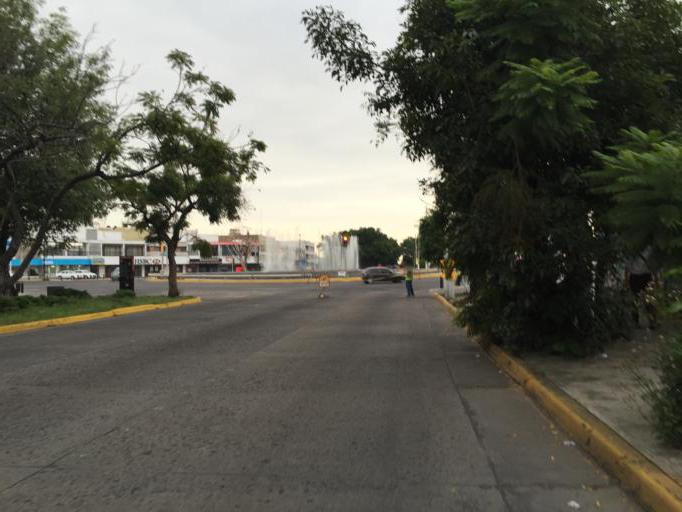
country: MX
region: Jalisco
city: Guadalajara
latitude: 20.6665
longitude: -103.3853
